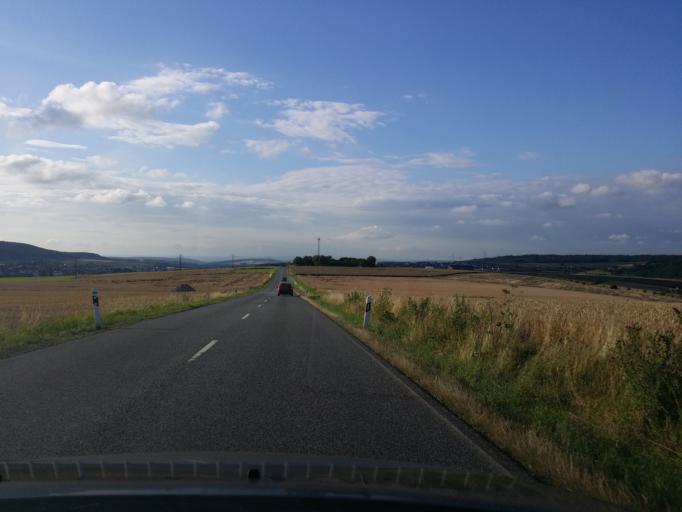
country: DE
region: Hesse
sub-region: Regierungsbezirk Darmstadt
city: Idstein
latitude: 50.2004
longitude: 8.2817
